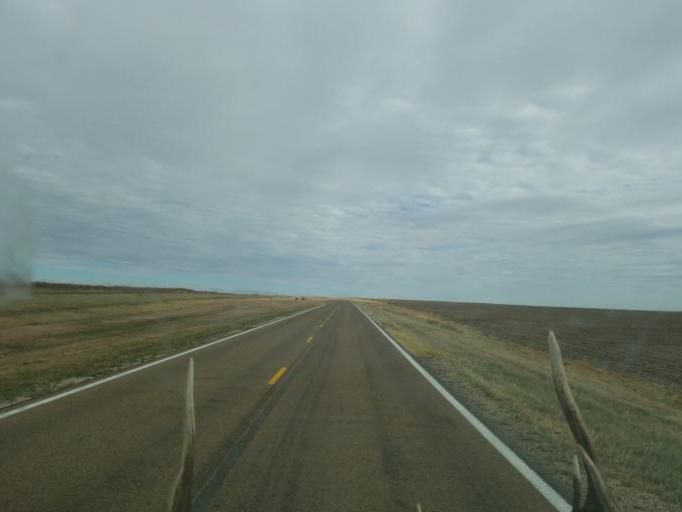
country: US
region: Kansas
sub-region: Thomas County
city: Colby
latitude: 39.0328
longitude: -101.2848
